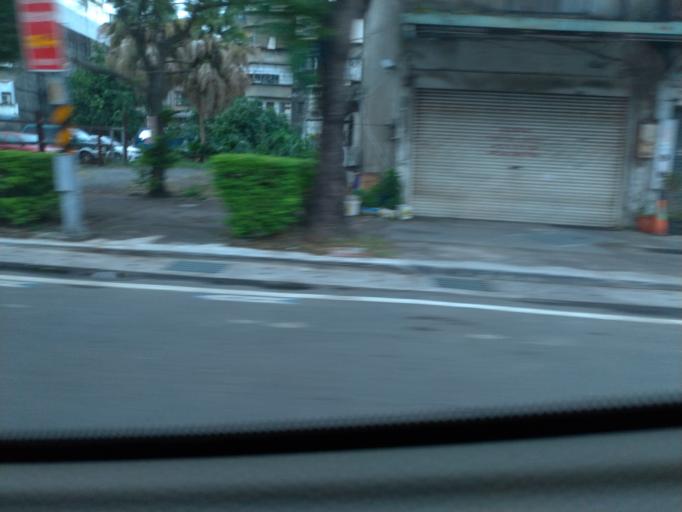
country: TW
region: Taiwan
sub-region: Taoyuan
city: Taoyuan
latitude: 24.9310
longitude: 121.3771
